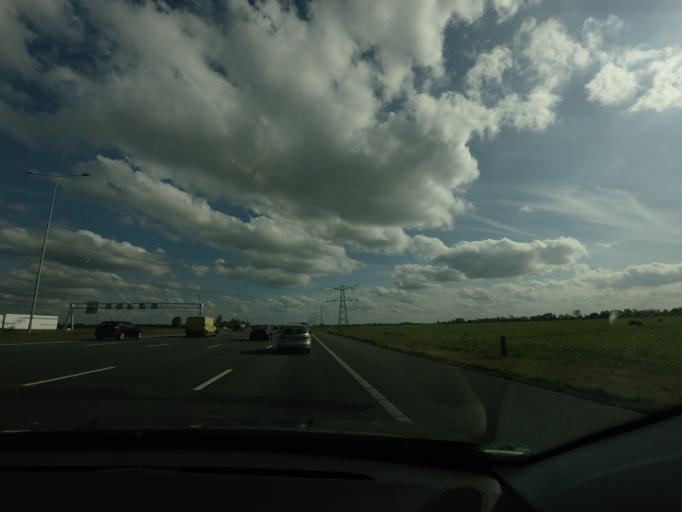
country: NL
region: Utrecht
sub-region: Stichtse Vecht
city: Breukelen
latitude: 52.2117
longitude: 4.9861
